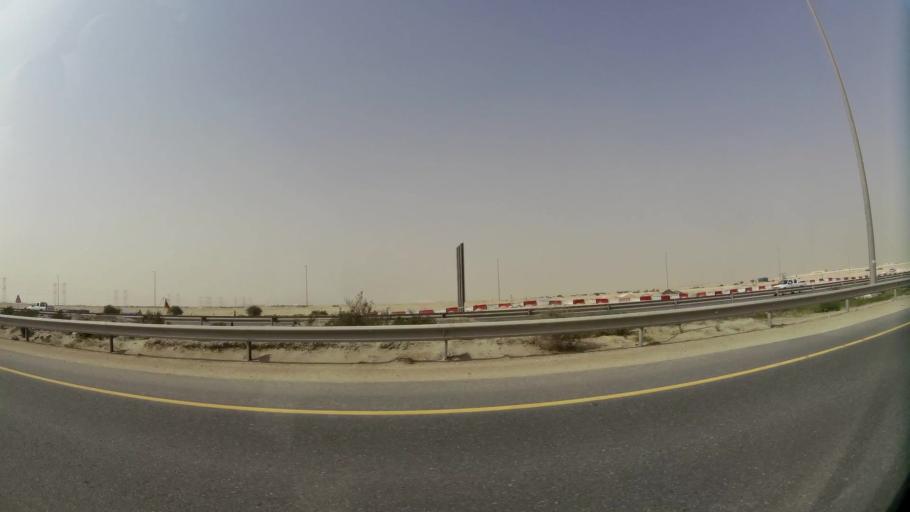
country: QA
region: Baladiyat ar Rayyan
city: Ar Rayyan
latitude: 25.1787
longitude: 51.3440
